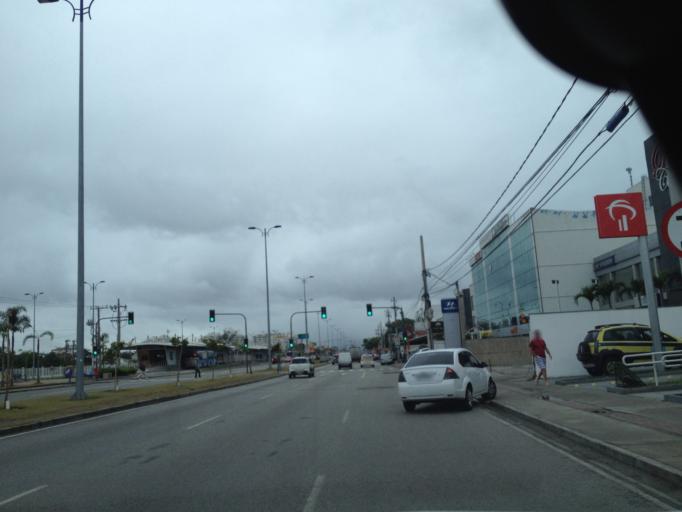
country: BR
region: Rio de Janeiro
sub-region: Nilopolis
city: Nilopolis
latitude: -23.0132
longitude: -43.4606
